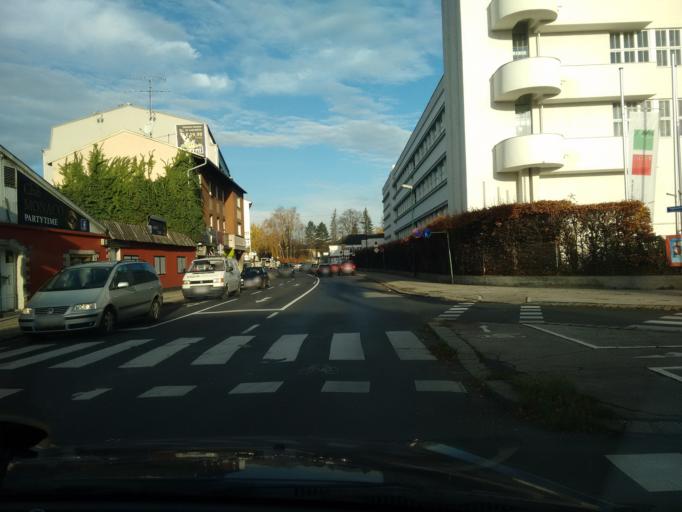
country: AT
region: Upper Austria
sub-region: Wels Stadt
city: Wels
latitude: 48.1604
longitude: 14.0190
